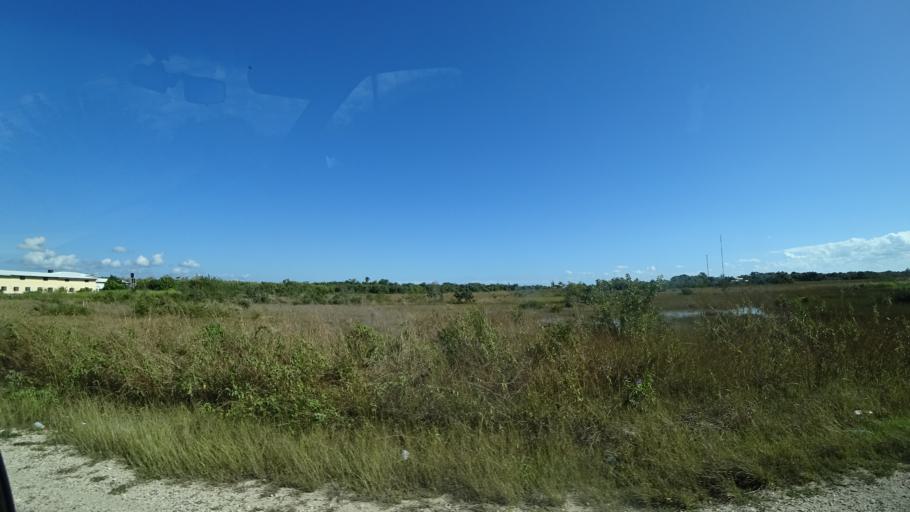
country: BZ
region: Belize
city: Belize City
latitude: 17.5607
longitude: -88.3214
